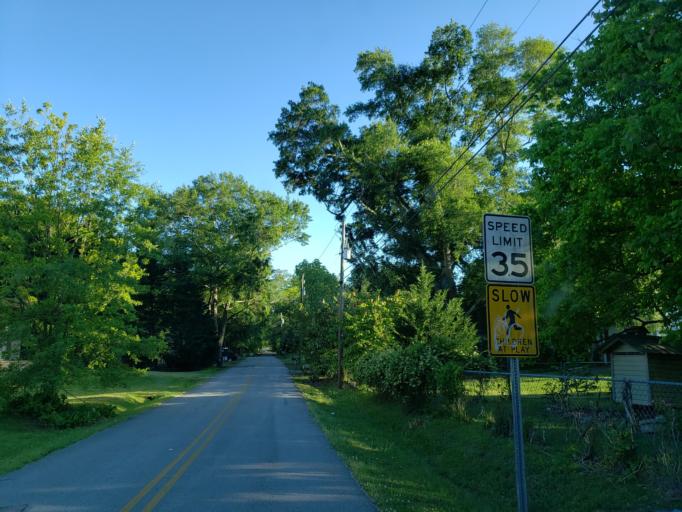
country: US
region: Georgia
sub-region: Haralson County
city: Tallapoosa
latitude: 33.7543
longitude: -85.2938
